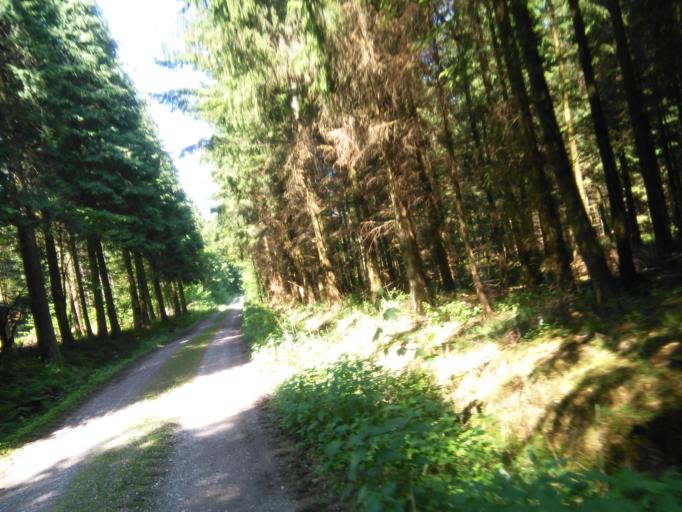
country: DK
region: Central Jutland
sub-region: Arhus Kommune
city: Solbjerg
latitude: 55.9535
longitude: 10.0502
